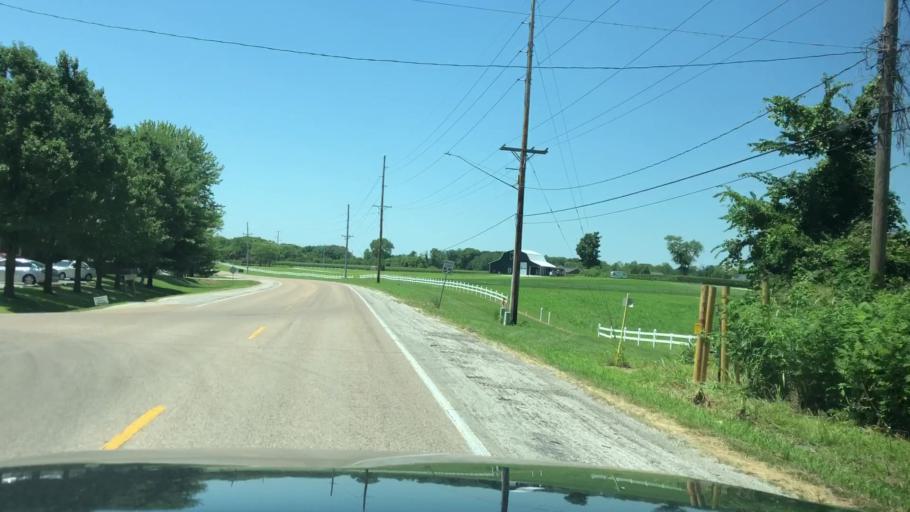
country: US
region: Illinois
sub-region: Saint Clair County
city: Centreville
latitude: 38.5444
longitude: -90.0817
